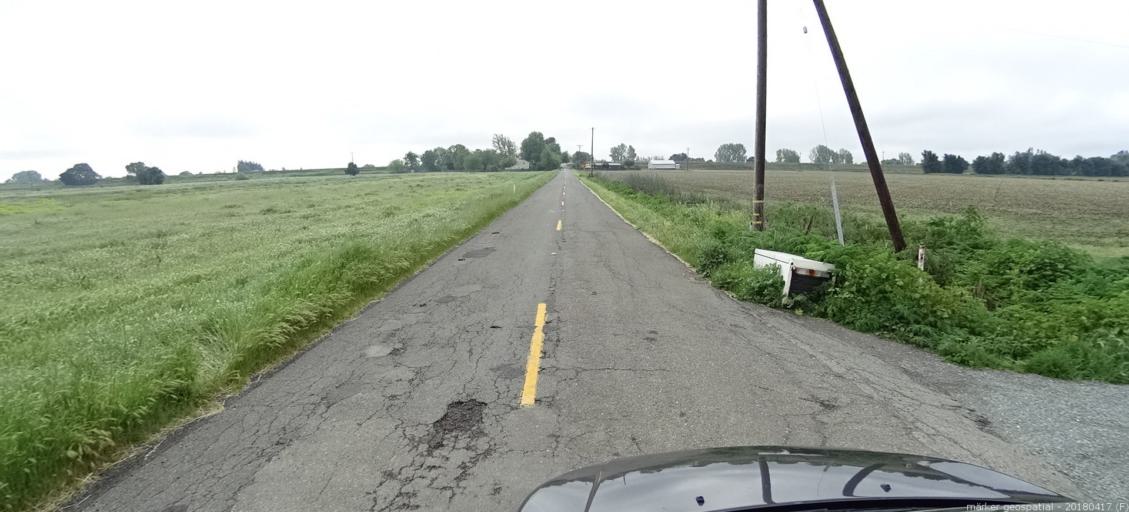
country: US
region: California
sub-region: Sacramento County
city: Walnut Grove
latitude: 38.1871
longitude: -121.5890
